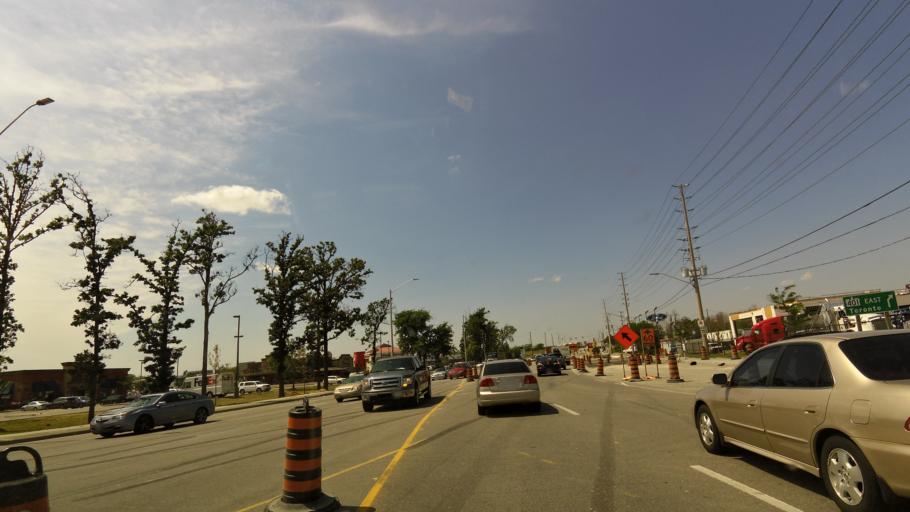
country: CA
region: Ontario
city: Etobicoke
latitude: 43.6446
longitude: -79.6328
